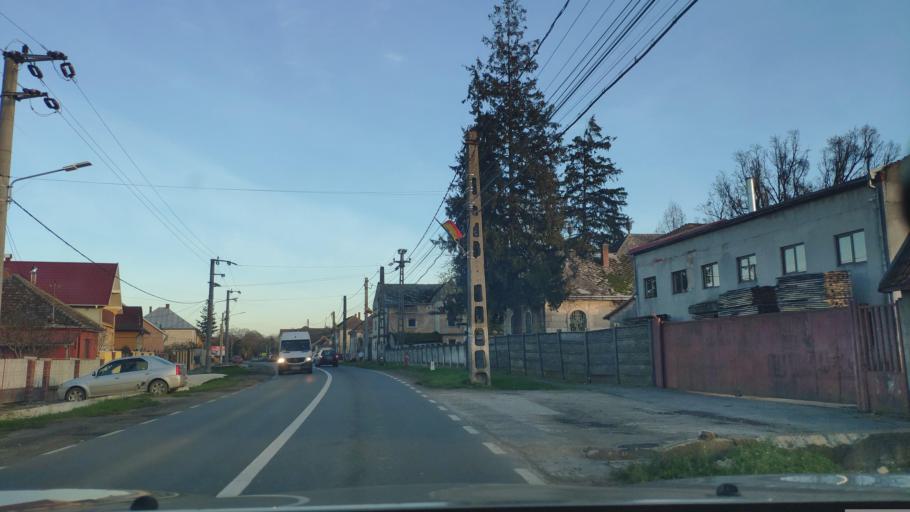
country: RO
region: Satu Mare
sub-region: Comuna Odoreu
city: Odoreu
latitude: 47.7957
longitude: 22.9865
